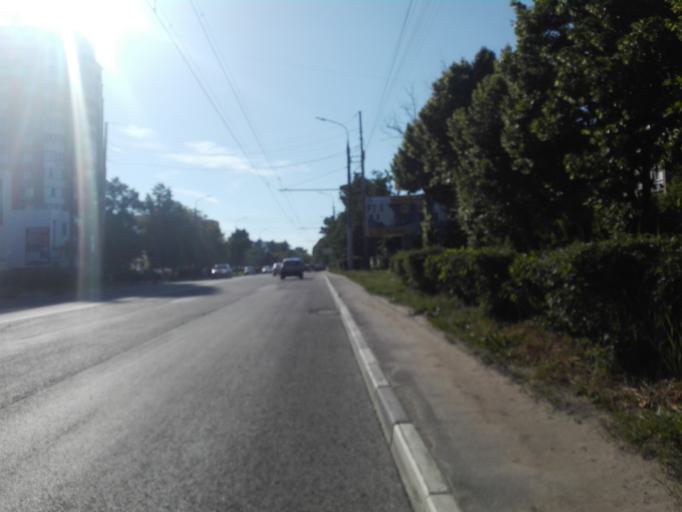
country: RU
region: Orjol
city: Orel
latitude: 52.9802
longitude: 36.0732
